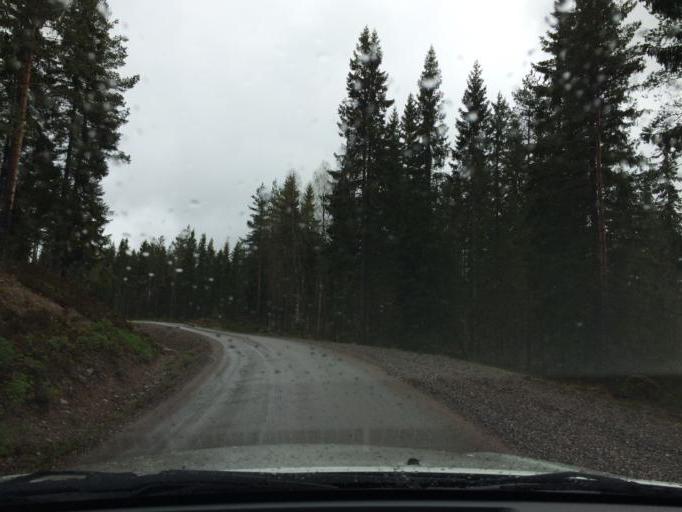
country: SE
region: OErebro
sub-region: Hallefors Kommun
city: Haellefors
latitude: 60.0197
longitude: 14.5676
